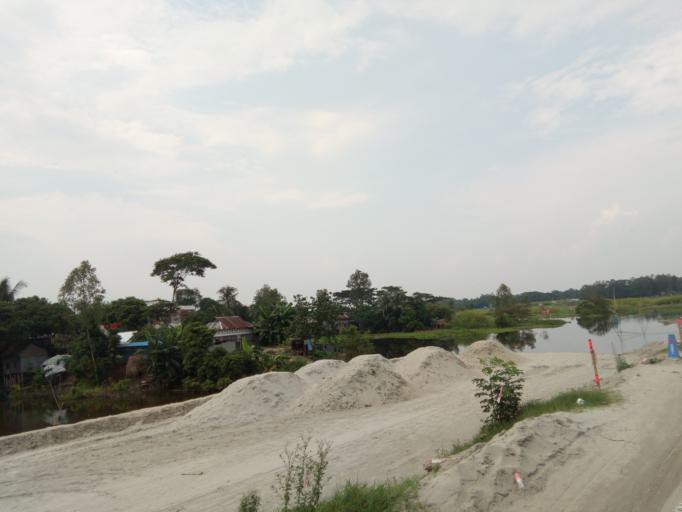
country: BD
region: Dhaka
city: Dohar
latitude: 23.5796
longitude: 90.3055
